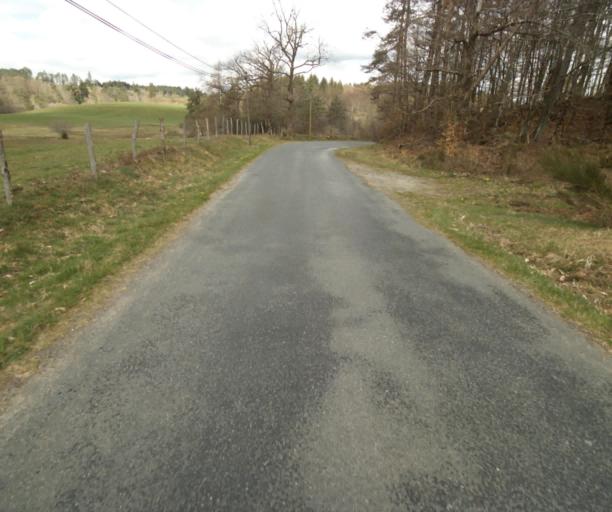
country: FR
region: Limousin
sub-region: Departement de la Correze
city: Correze
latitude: 45.3679
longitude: 1.9307
